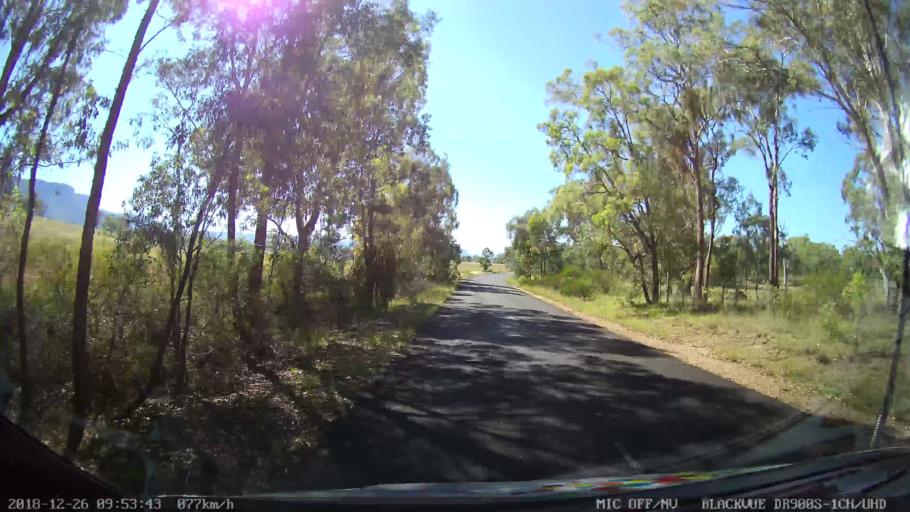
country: AU
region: New South Wales
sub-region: Mid-Western Regional
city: Kandos
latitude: -33.0236
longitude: 150.1551
